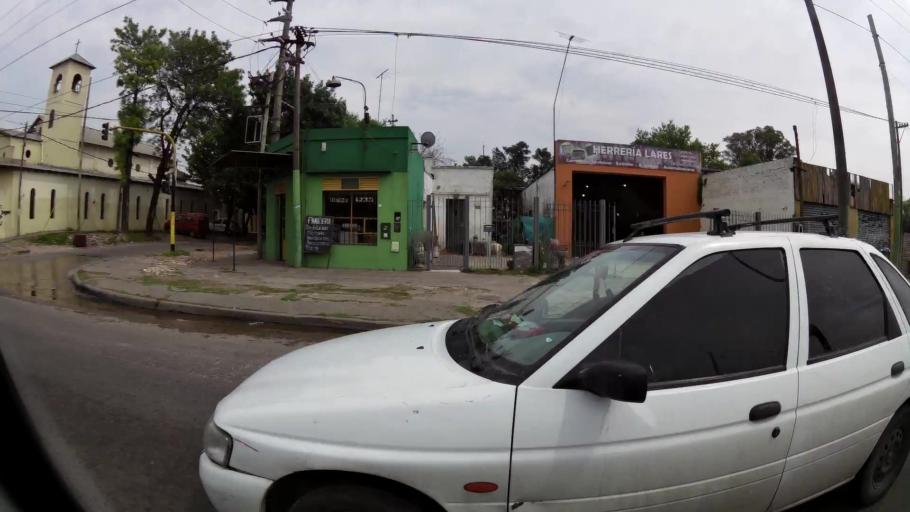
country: AR
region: Buenos Aires
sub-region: Partido de La Plata
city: La Plata
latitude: -34.9226
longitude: -58.0179
